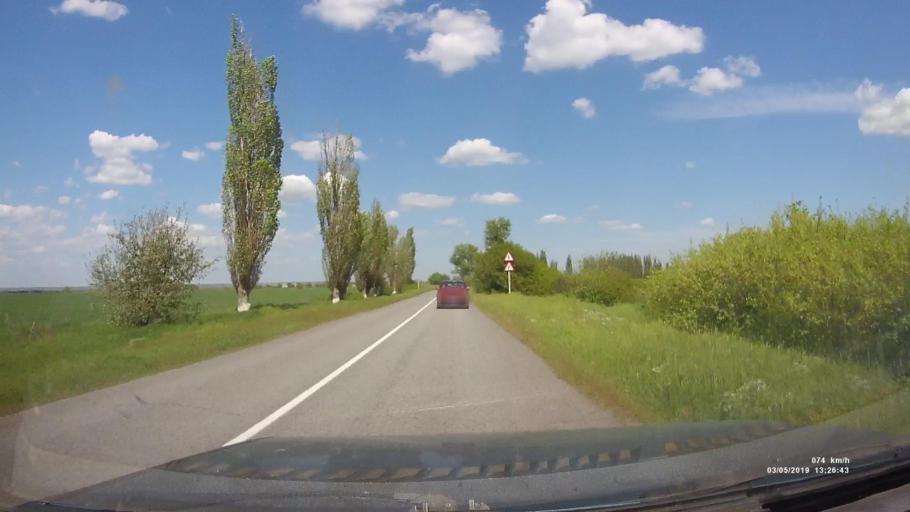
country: RU
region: Rostov
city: Semikarakorsk
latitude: 47.5729
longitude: 40.8247
